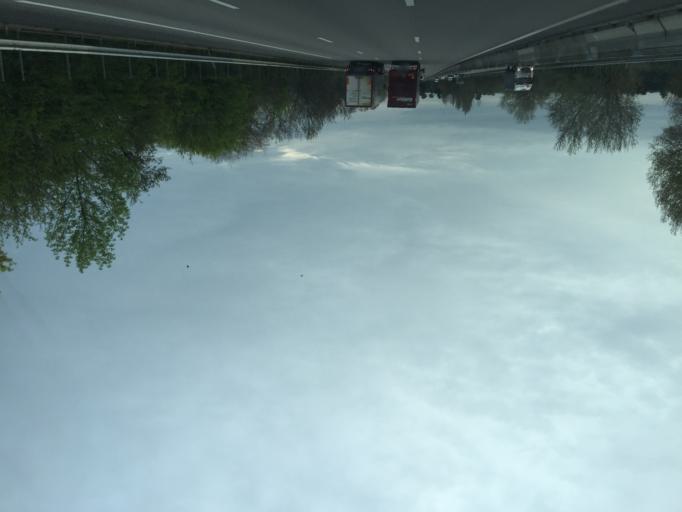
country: FR
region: Rhone-Alpes
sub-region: Departement de la Drome
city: La Roche-de-Glun
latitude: 44.9947
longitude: 4.8787
